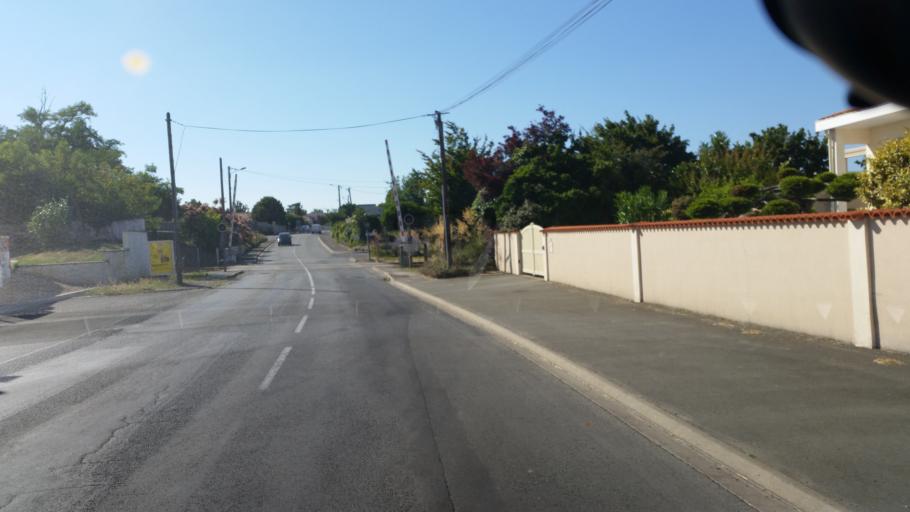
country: FR
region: Poitou-Charentes
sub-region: Departement de la Charente-Maritime
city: Marans
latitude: 46.3032
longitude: -0.9851
